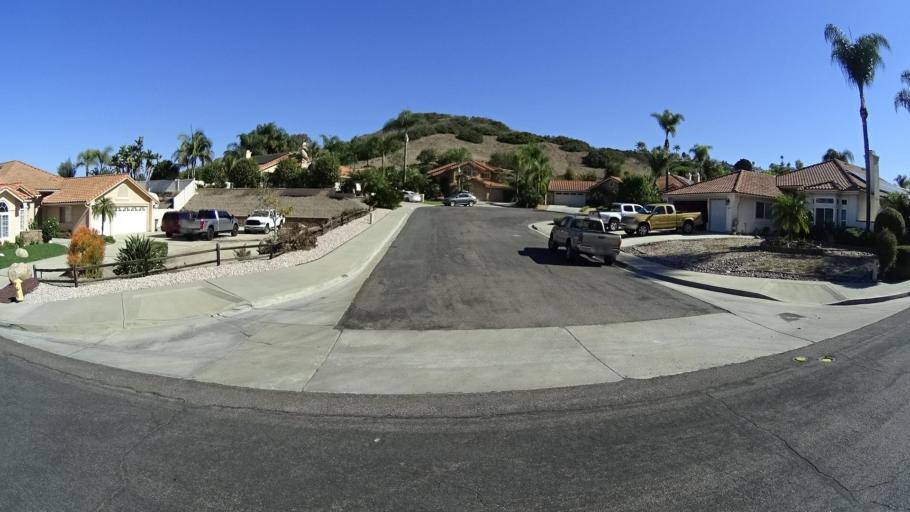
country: US
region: California
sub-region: San Diego County
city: Bonita
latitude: 32.6628
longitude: -117.0135
